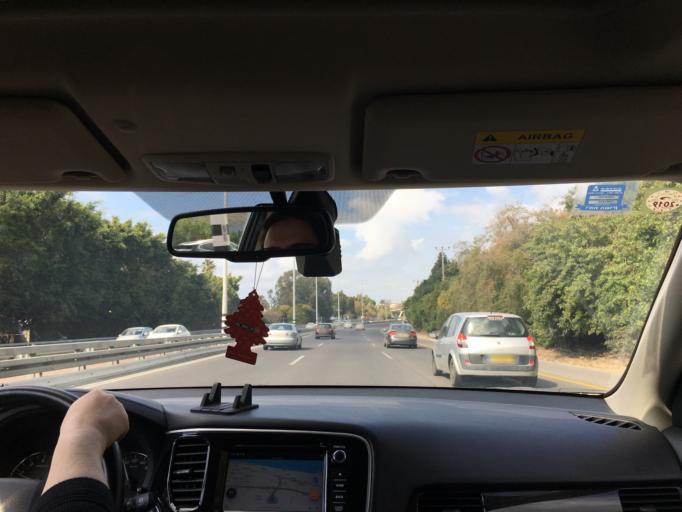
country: IL
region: Tel Aviv
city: Herzliyya
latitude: 32.1681
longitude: 34.8142
